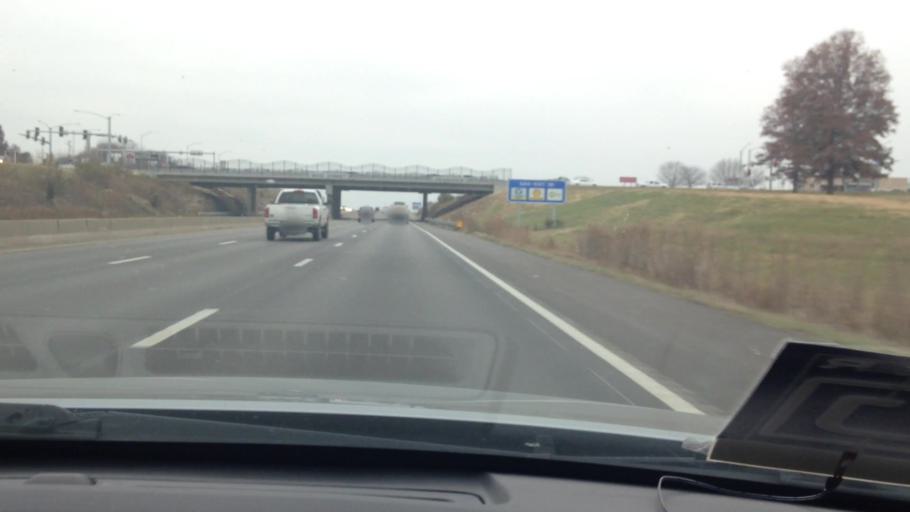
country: US
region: Missouri
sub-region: Jackson County
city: Grandview
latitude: 38.8873
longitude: -94.5252
